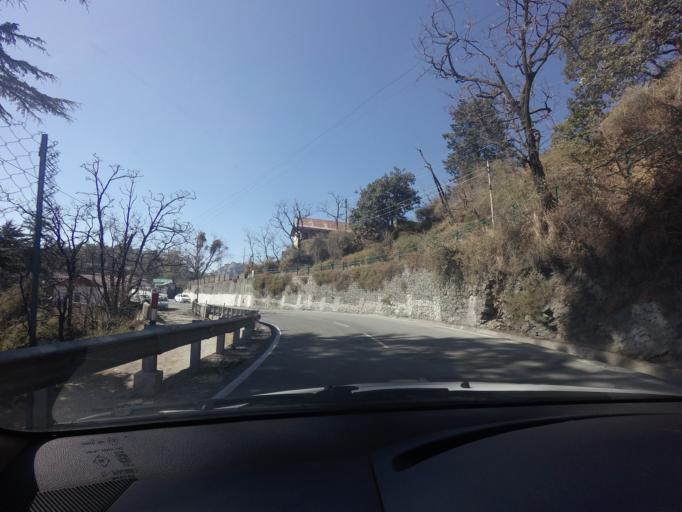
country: IN
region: Himachal Pradesh
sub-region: Shimla
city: Shimla
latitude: 31.1115
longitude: 77.2194
